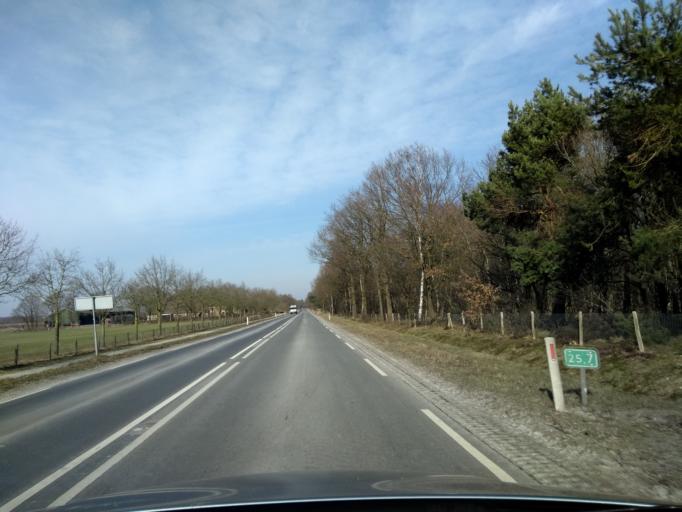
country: DE
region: Lower Saxony
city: Wielen
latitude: 52.4749
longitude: 6.6998
